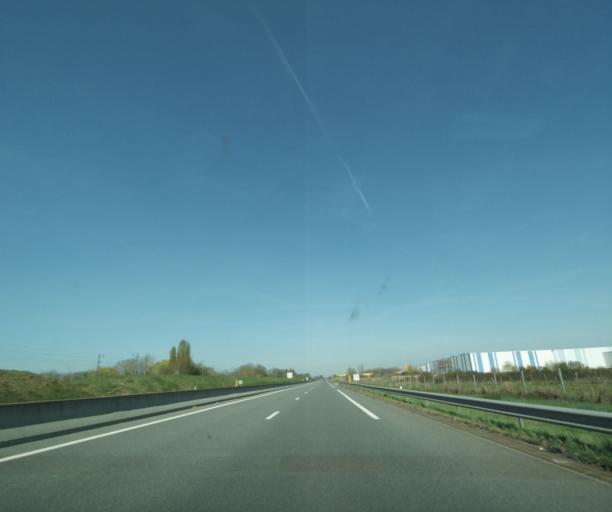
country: FR
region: Auvergne
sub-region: Departement de l'Allier
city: Avermes
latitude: 46.6062
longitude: 3.2970
